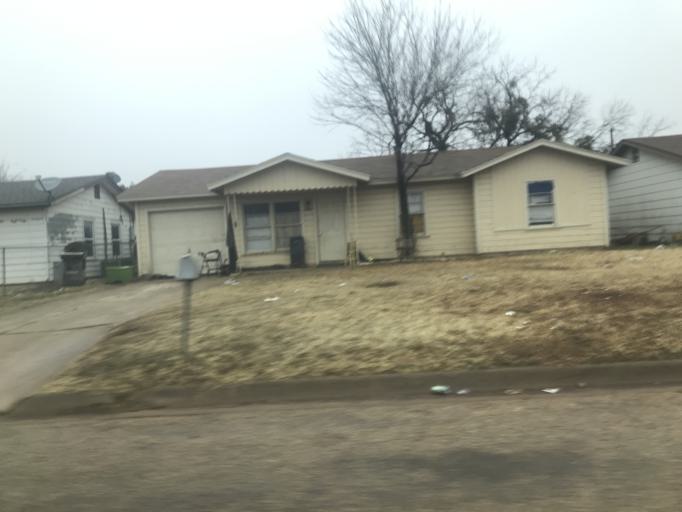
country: US
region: Texas
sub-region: Taylor County
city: Abilene
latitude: 32.4450
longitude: -99.7928
